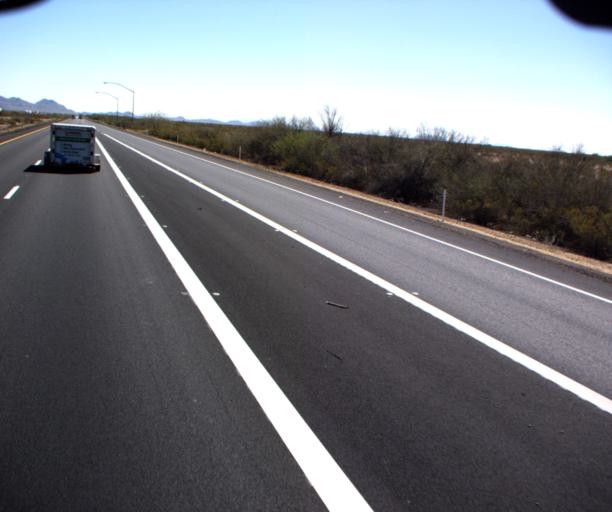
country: US
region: Arizona
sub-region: La Paz County
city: Salome
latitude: 33.6299
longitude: -113.7625
